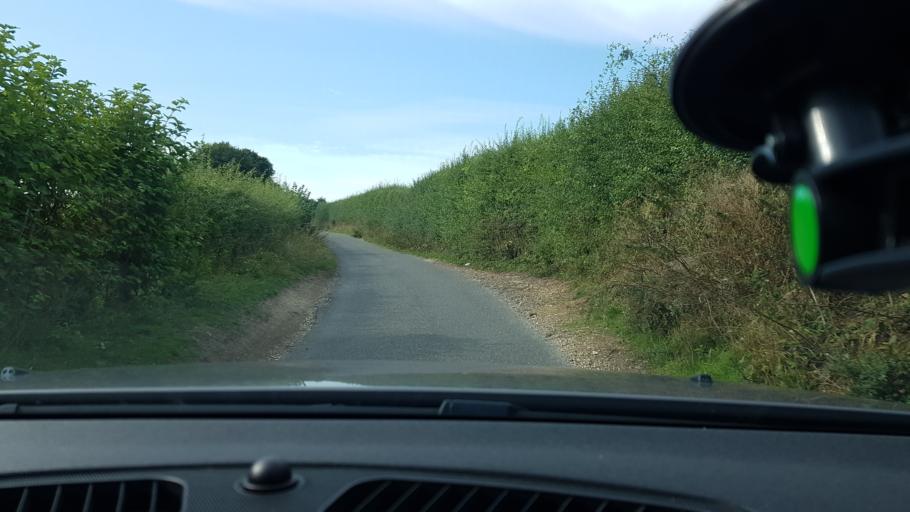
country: GB
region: England
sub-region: West Berkshire
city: Wickham
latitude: 51.4252
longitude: -1.4468
